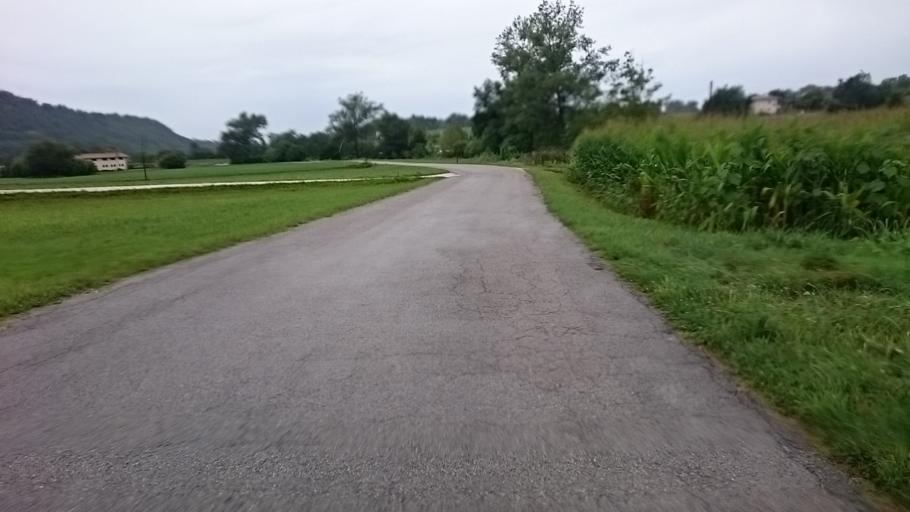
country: IT
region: Veneto
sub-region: Provincia di Treviso
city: Monfumo
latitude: 45.8206
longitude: 11.9092
